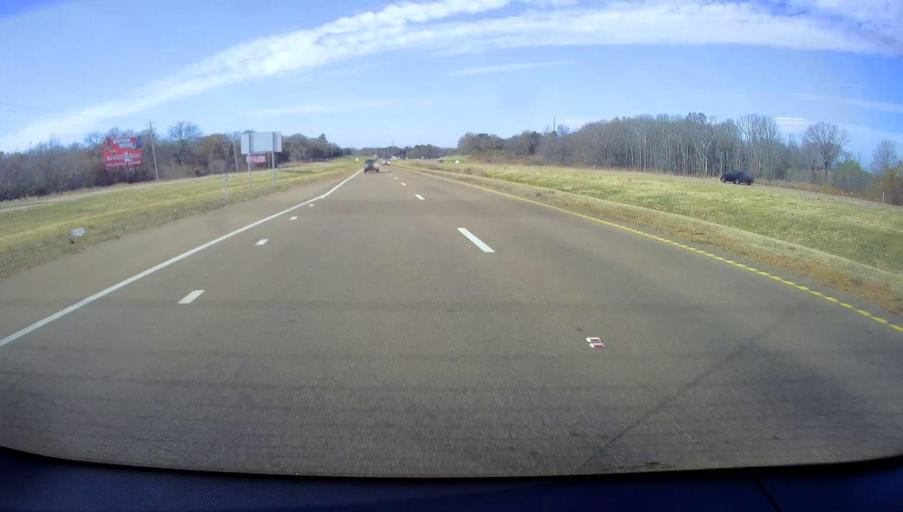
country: US
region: Tennessee
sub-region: Fayette County
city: Piperton
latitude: 34.9873
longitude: -89.6033
